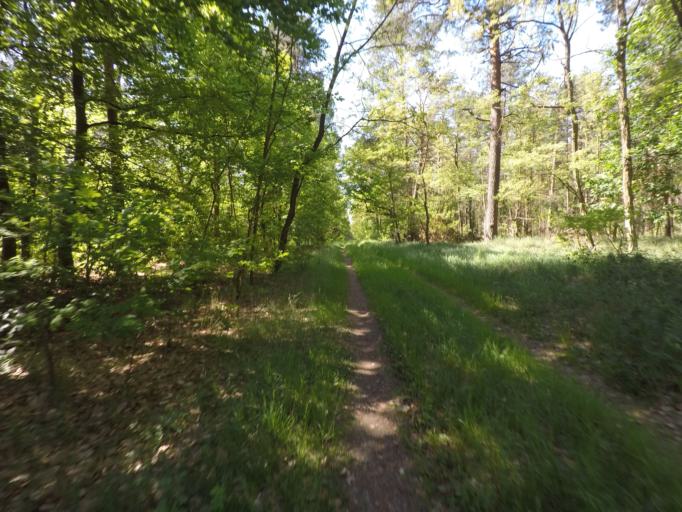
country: DE
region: Brandenburg
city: Eberswalde
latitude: 52.8165
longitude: 13.7639
